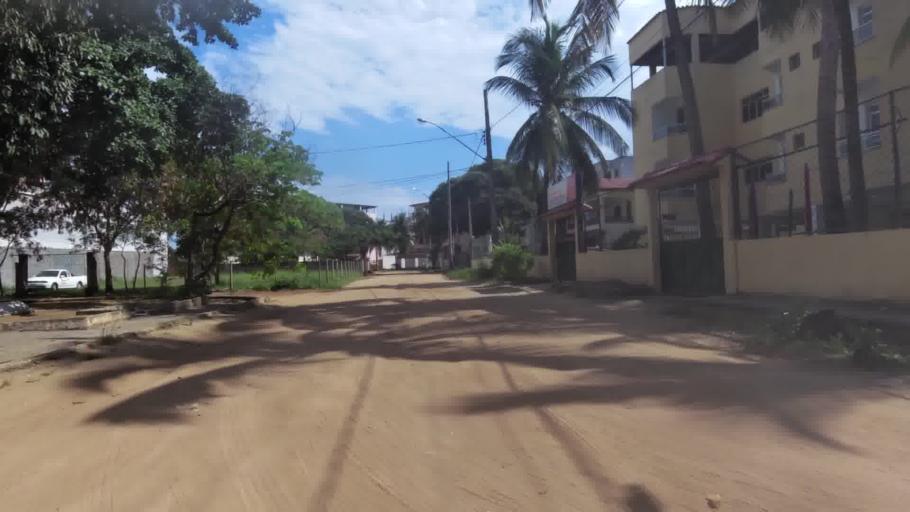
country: BR
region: Espirito Santo
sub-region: Piuma
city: Piuma
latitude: -20.8428
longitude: -40.7345
